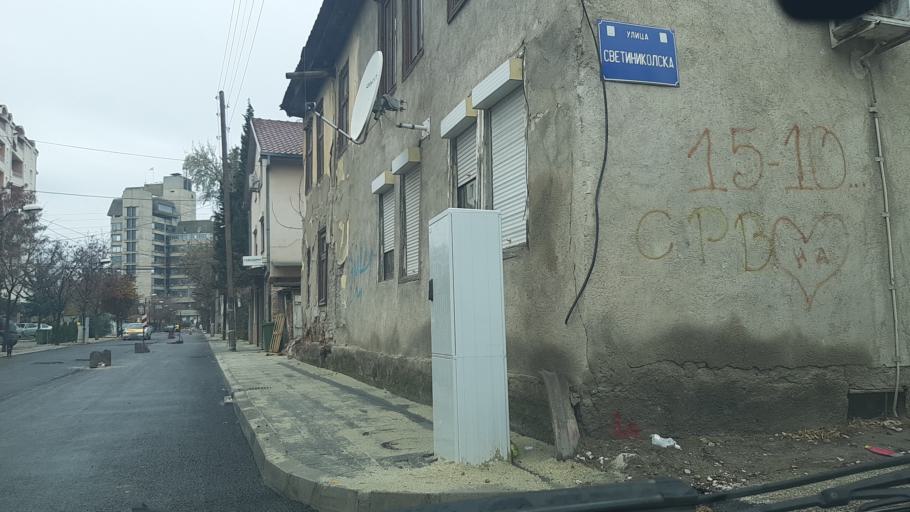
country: MK
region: Karpos
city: Skopje
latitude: 41.9933
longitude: 21.4464
